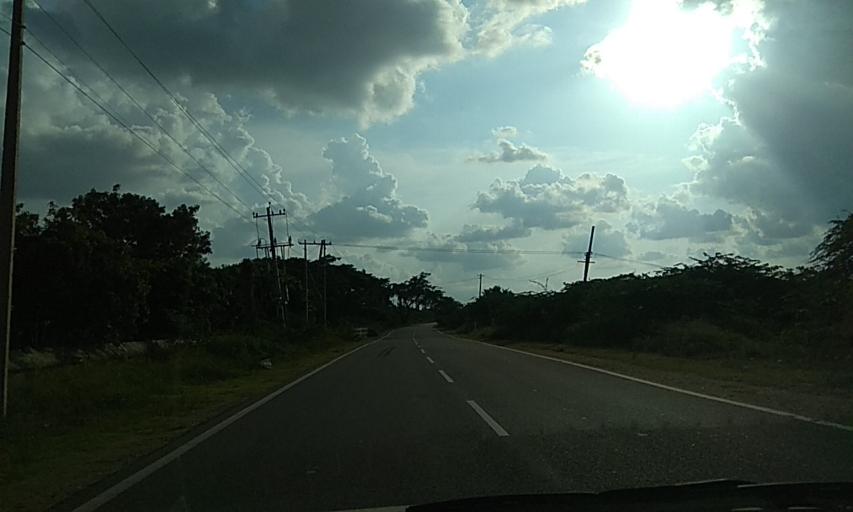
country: IN
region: Karnataka
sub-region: Chamrajnagar
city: Gundlupet
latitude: 11.8129
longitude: 76.7777
